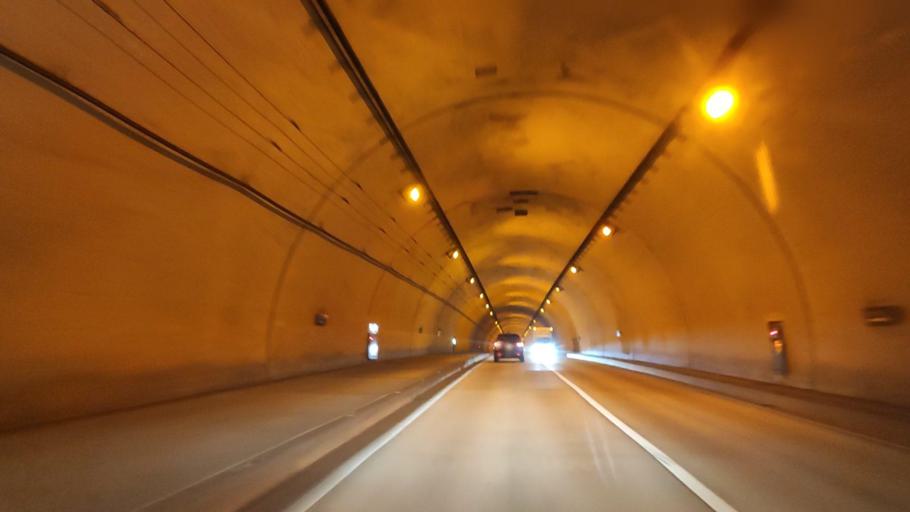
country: JP
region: Ehime
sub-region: Shikoku-chuo Shi
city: Matsuyama
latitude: 33.8821
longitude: 132.7104
